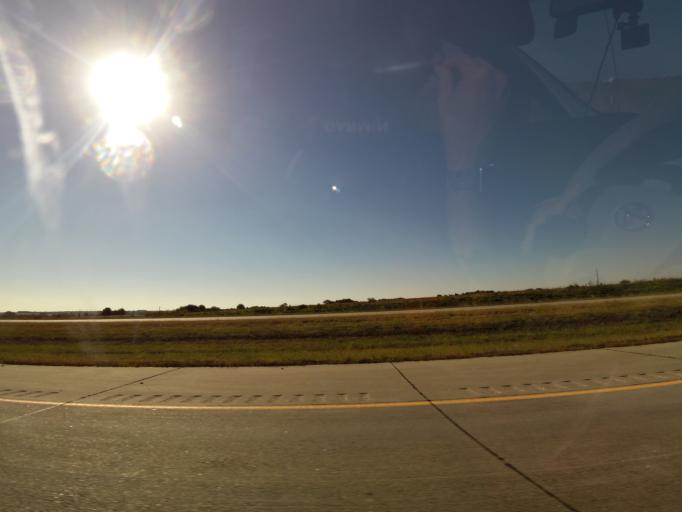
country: US
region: Nebraska
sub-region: Lancaster County
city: Waverly
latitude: 40.9091
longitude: -96.4941
